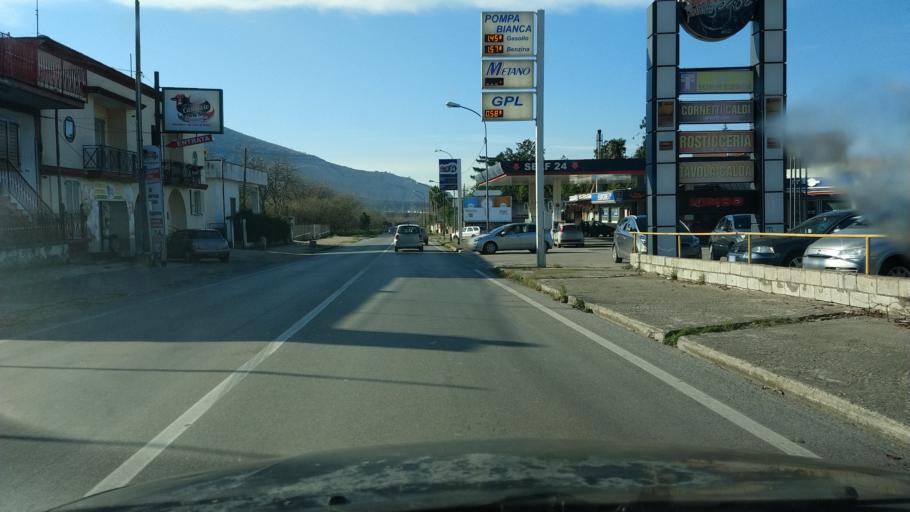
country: IT
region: Campania
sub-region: Provincia di Avellino
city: Avella
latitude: 40.9514
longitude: 14.5890
